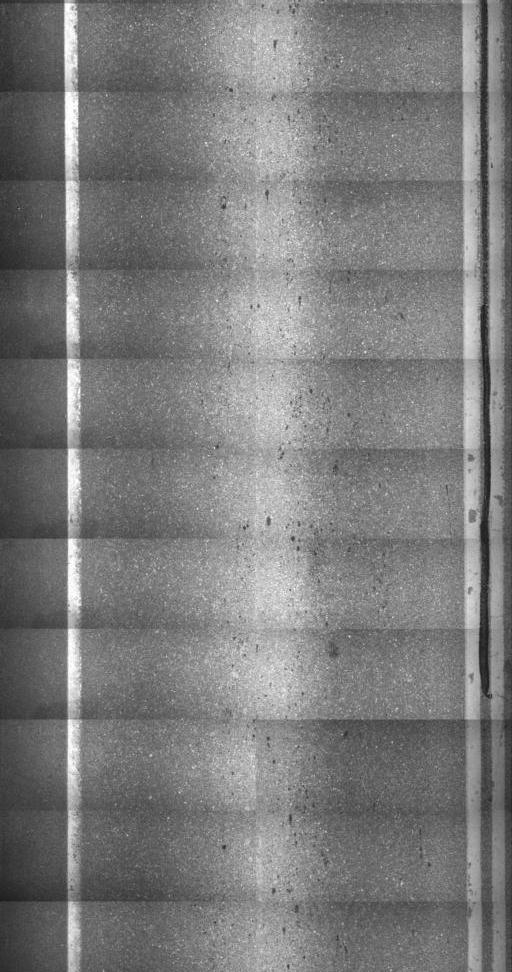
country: US
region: Vermont
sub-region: Chittenden County
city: Milton
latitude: 44.6107
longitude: -73.0093
